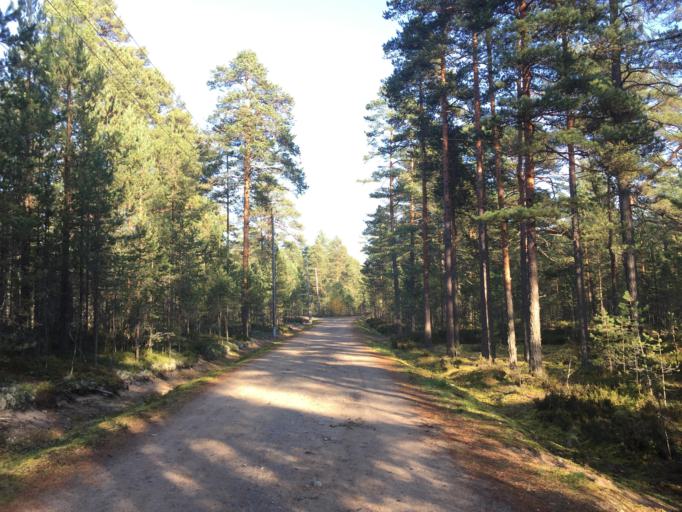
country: RU
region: Leningrad
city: Priozersk
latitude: 61.2806
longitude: 30.1001
